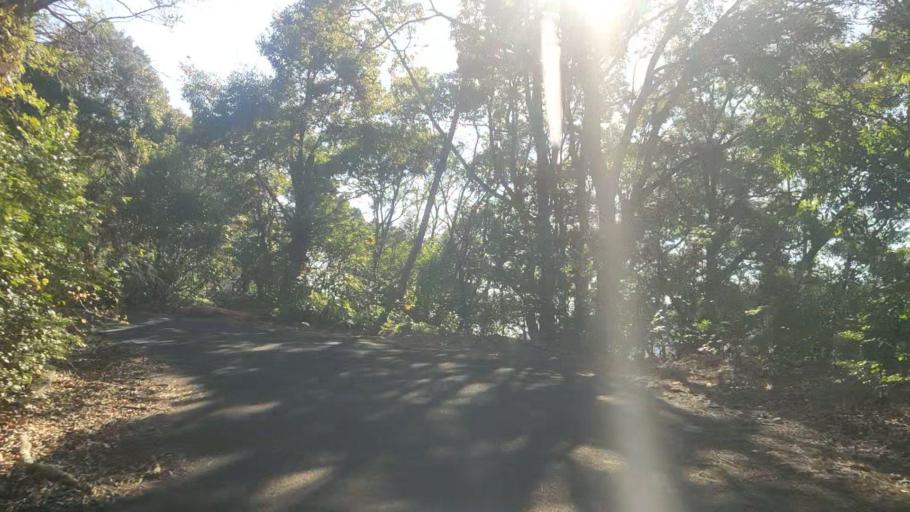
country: JP
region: Oita
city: Saiki
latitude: 32.7852
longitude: 131.8534
